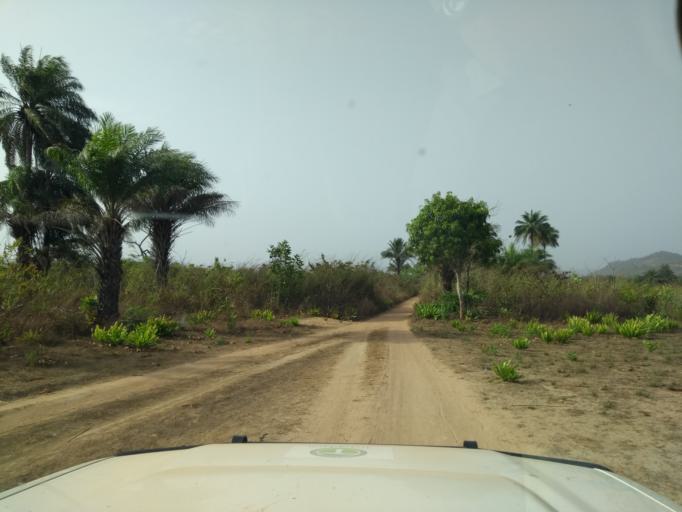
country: GN
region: Kindia
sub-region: Prefecture de Dubreka
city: Dubreka
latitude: 9.8250
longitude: -13.5554
